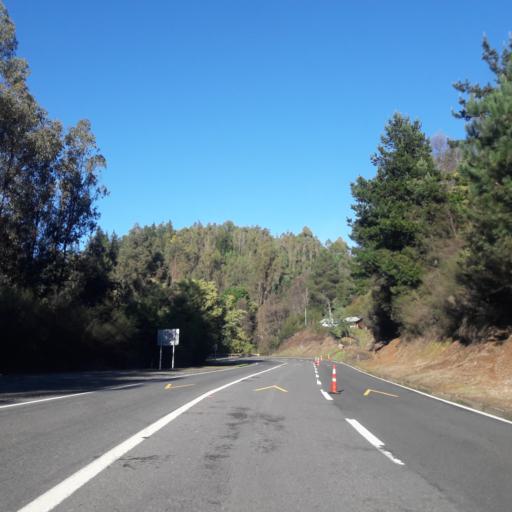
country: CL
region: Biobio
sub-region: Provincia de Biobio
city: La Laja
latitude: -37.2602
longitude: -72.9607
